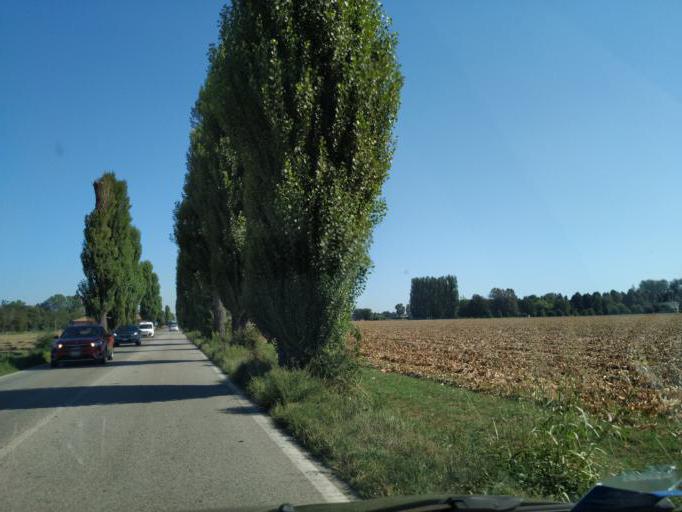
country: IT
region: Emilia-Romagna
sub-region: Provincia di Ferrara
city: Cento
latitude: 44.7289
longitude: 11.2604
